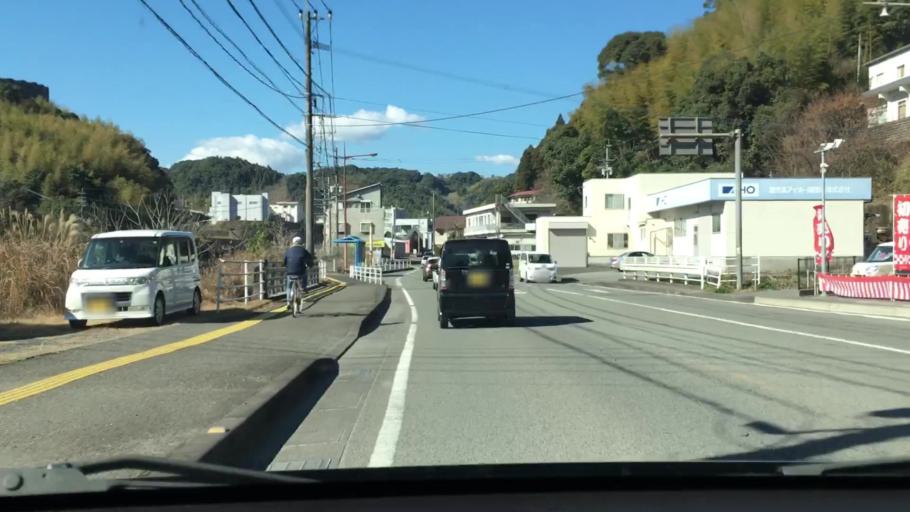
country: JP
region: Kagoshima
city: Kagoshima-shi
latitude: 31.6389
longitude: 130.5188
